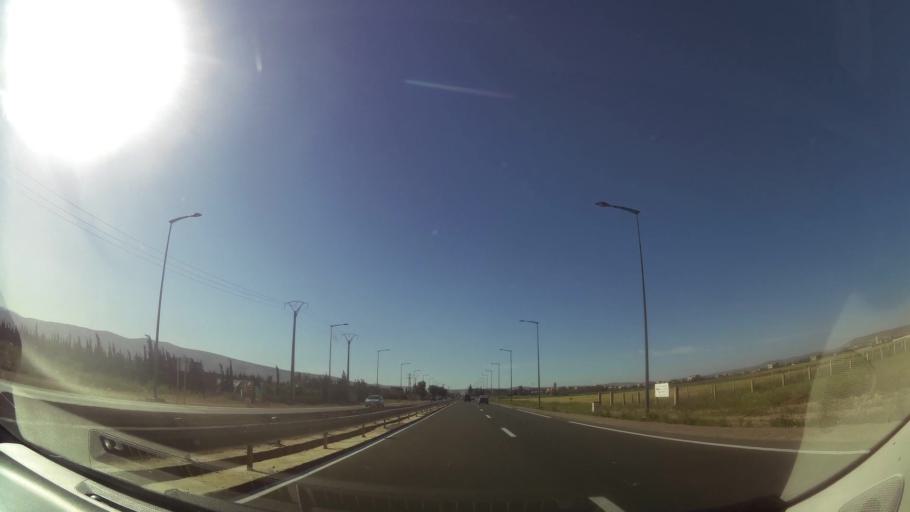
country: MA
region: Oriental
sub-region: Berkane-Taourirt
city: Ahfir
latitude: 34.8482
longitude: -1.9862
